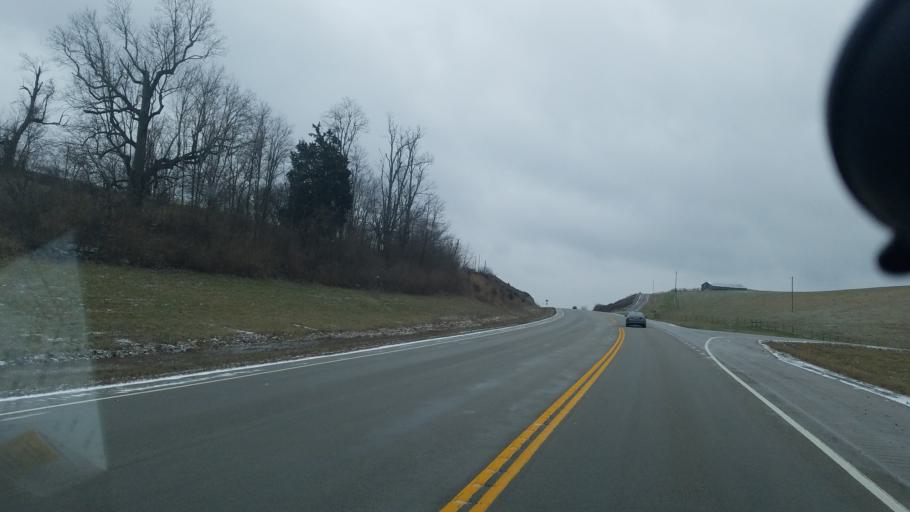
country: US
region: Kentucky
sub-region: Fleming County
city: Flemingsburg
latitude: 38.3348
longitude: -83.7728
